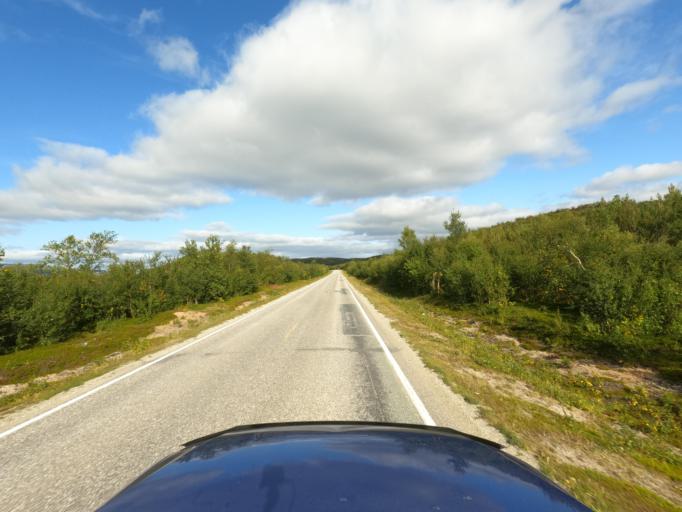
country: NO
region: Finnmark Fylke
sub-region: Porsanger
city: Lakselv
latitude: 69.9643
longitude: 24.9668
